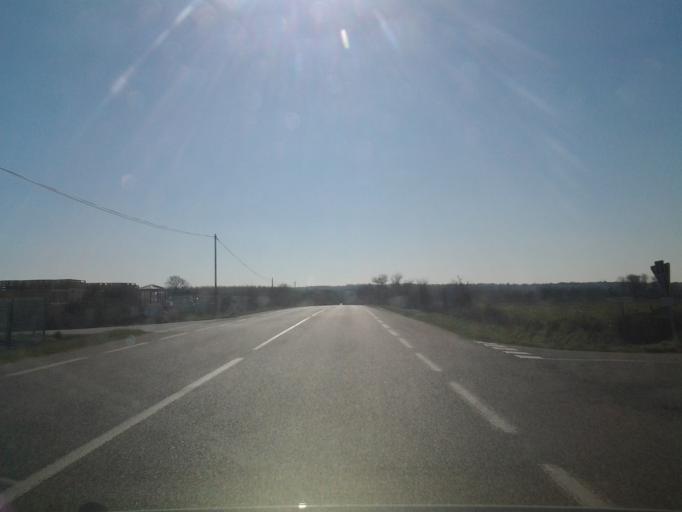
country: FR
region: Pays de la Loire
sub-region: Departement de la Vendee
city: Saint-Mathurin
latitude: 46.5559
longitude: -1.7226
